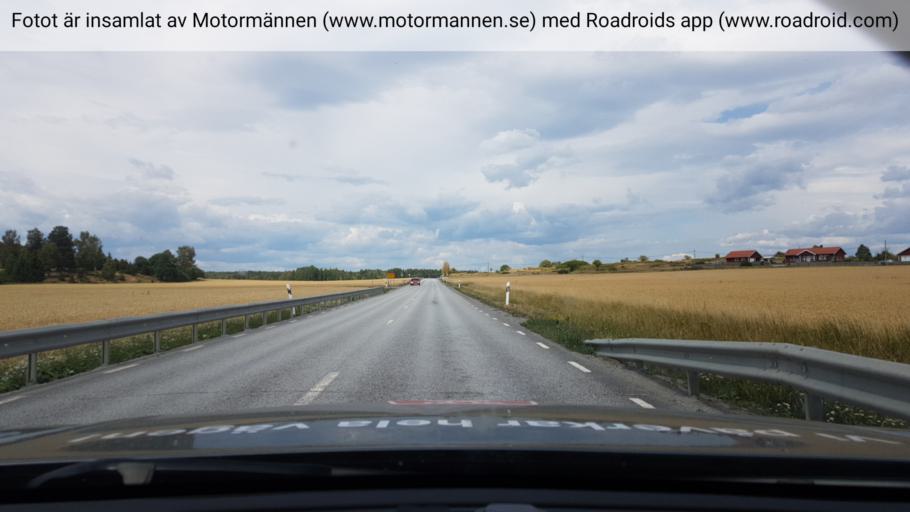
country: SE
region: Uppsala
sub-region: Habo Kommun
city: Balsta
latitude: 59.6219
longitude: 17.6050
